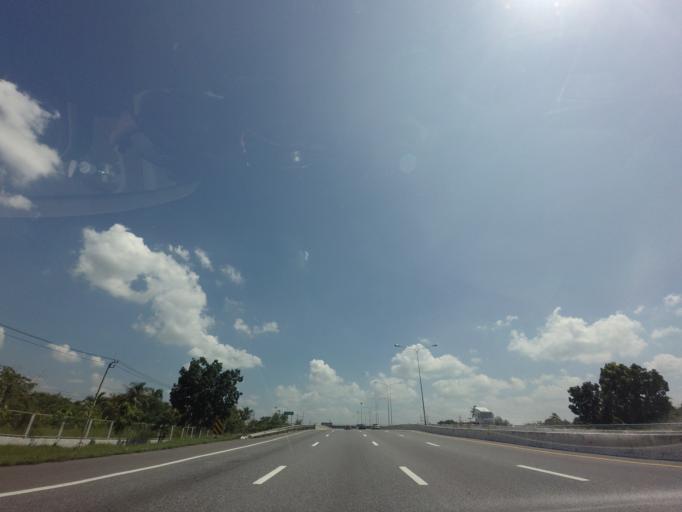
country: TH
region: Chachoengsao
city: Bang Pakong
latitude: 13.6107
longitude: 100.9364
